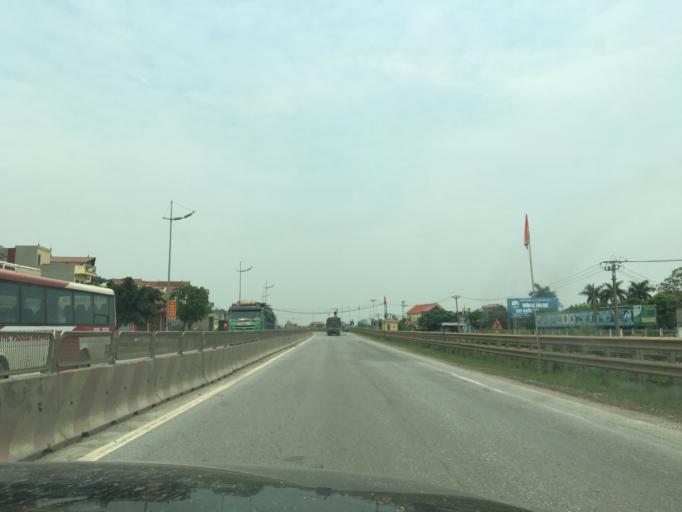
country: VN
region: Ninh Binh
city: Thi Tran Tam Diep
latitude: 20.1647
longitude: 105.9359
